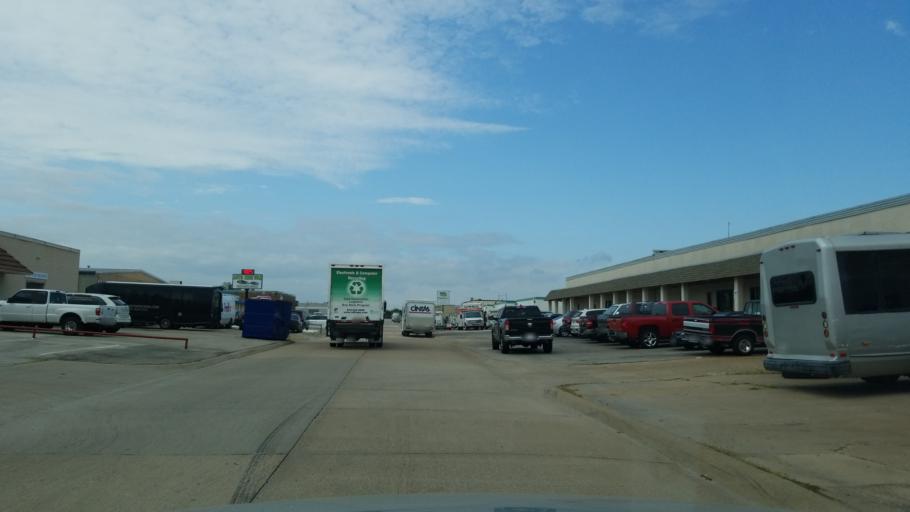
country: US
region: Texas
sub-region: Dallas County
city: Garland
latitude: 32.8988
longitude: -96.6855
